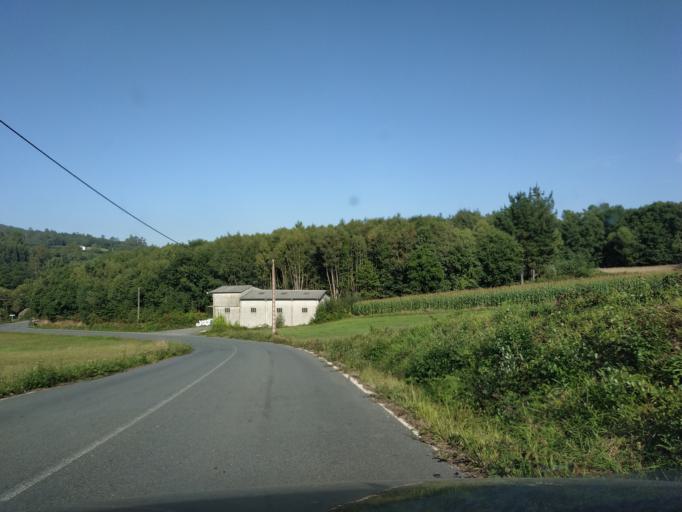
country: ES
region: Galicia
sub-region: Provincia da Coruna
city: Cerceda
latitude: 43.2312
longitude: -8.4899
